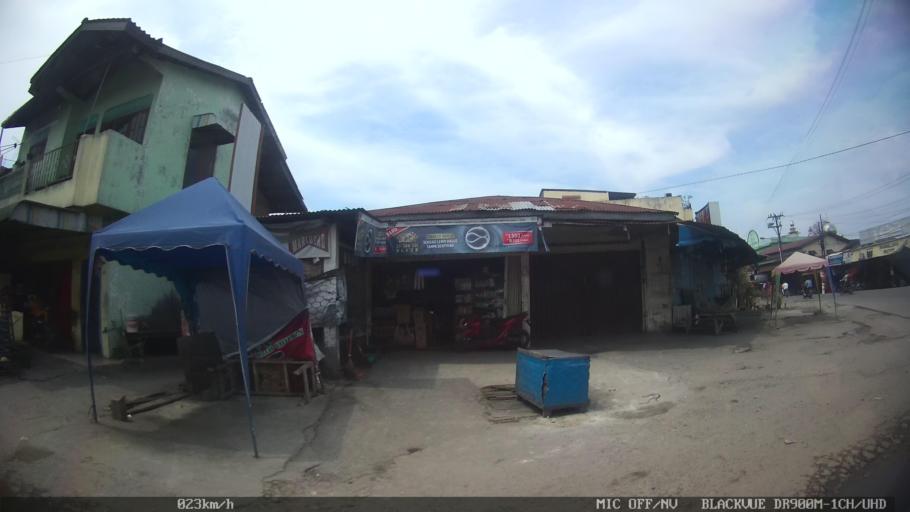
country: ID
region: North Sumatra
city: Labuhan Deli
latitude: 3.6571
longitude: 98.6762
